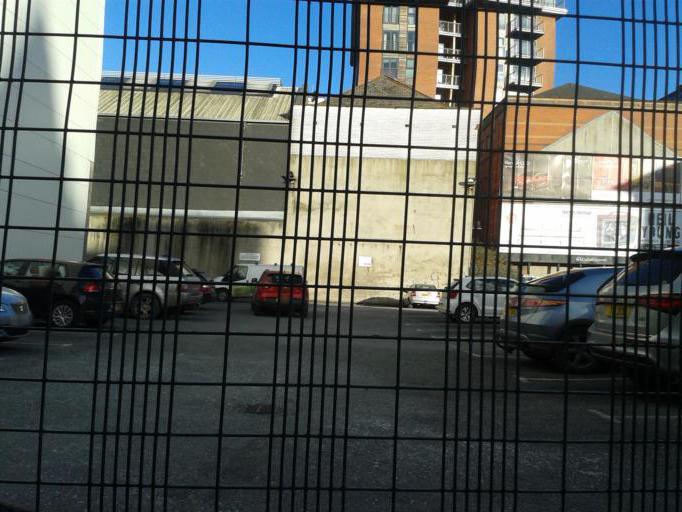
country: GB
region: Northern Ireland
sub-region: City of Belfast
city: Belfast
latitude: 54.5978
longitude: -5.9278
